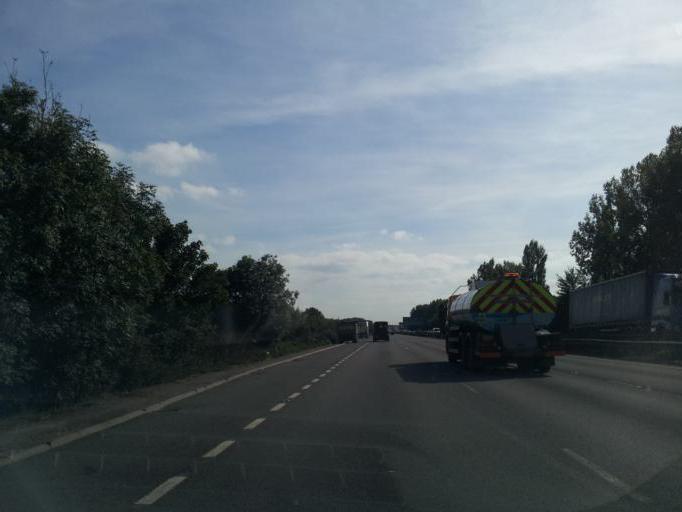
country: GB
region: England
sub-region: Cambridgeshire
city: Girton
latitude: 52.2527
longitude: 0.0337
